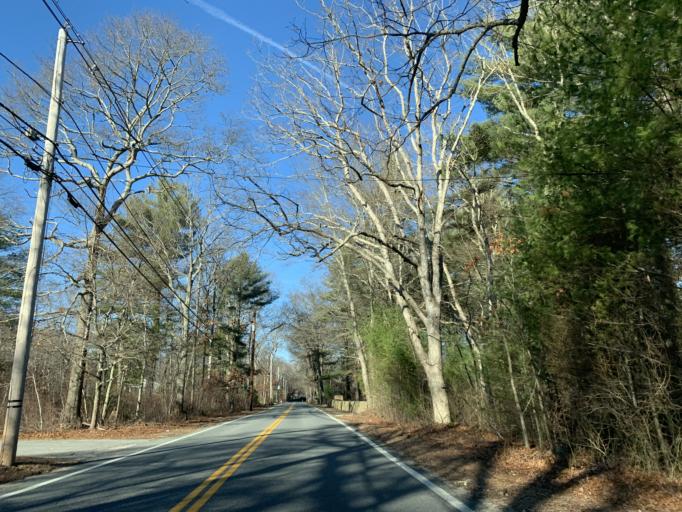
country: US
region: Rhode Island
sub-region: Washington County
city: Exeter
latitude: 41.5653
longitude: -71.5362
